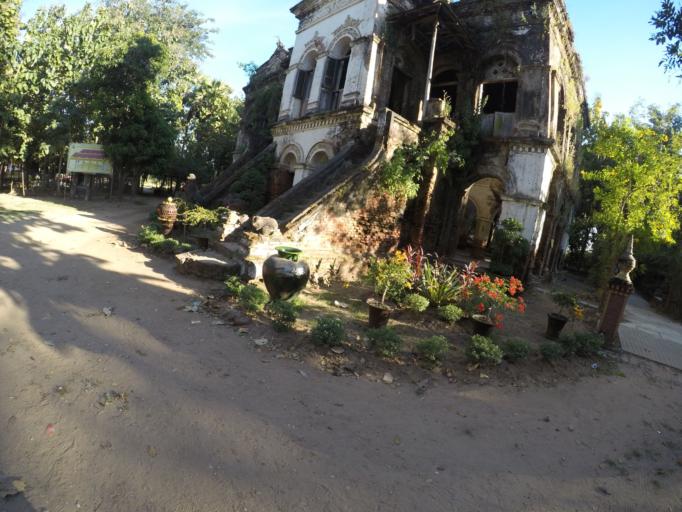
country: MM
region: Bago
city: Pyay
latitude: 18.7870
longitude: 95.3162
